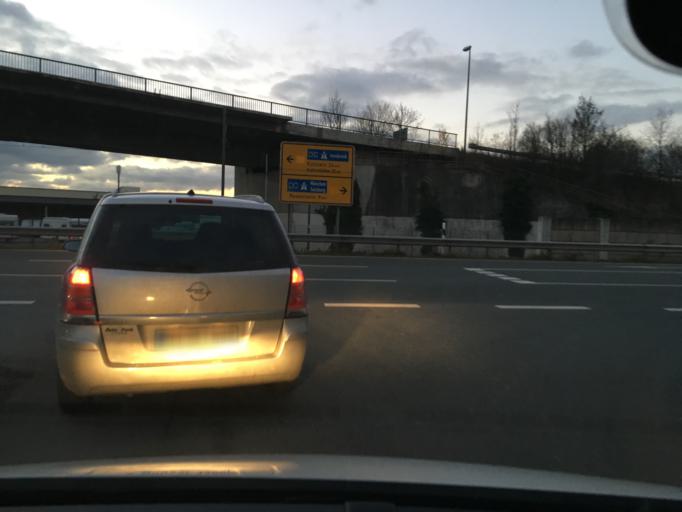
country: DE
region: Bavaria
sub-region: Upper Bavaria
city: Raubling
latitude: 47.7838
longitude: 12.1070
